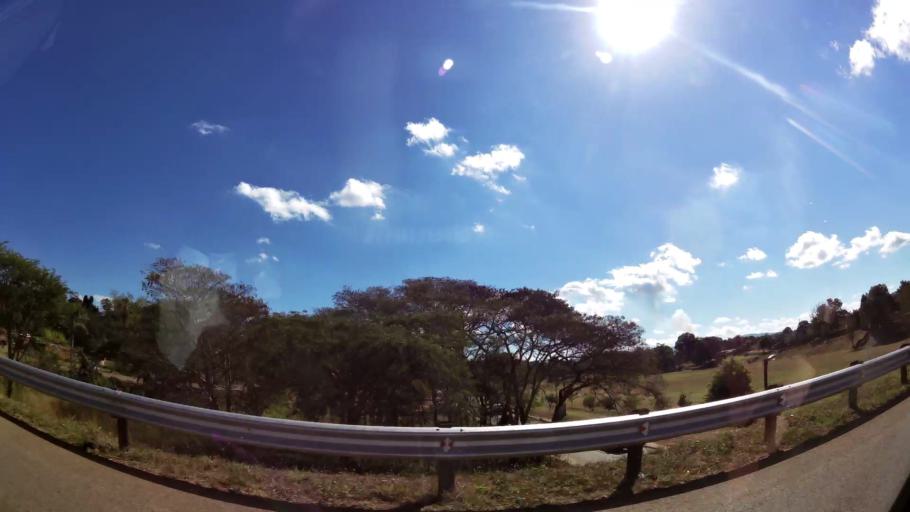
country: ZA
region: Limpopo
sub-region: Mopani District Municipality
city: Tzaneen
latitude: -23.8211
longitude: 30.1622
